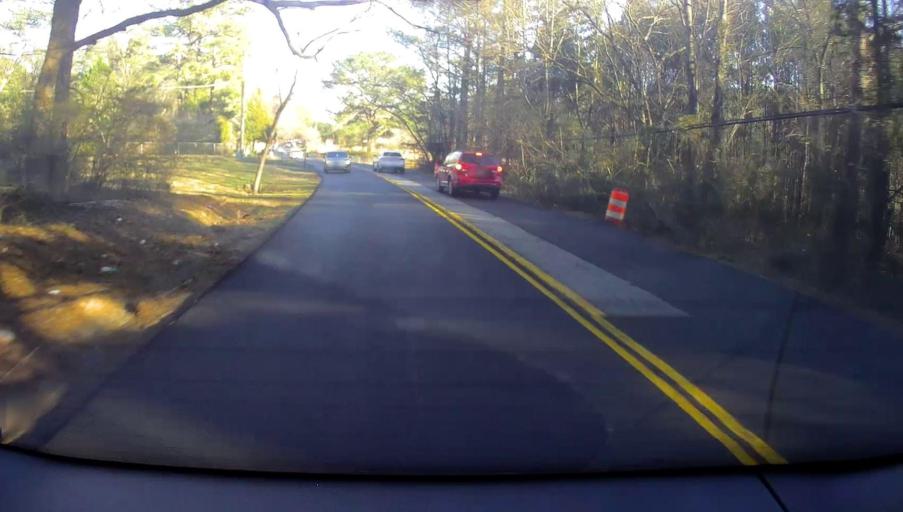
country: US
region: Georgia
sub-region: Clayton County
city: Irondale
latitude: 33.4549
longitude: -84.3763
